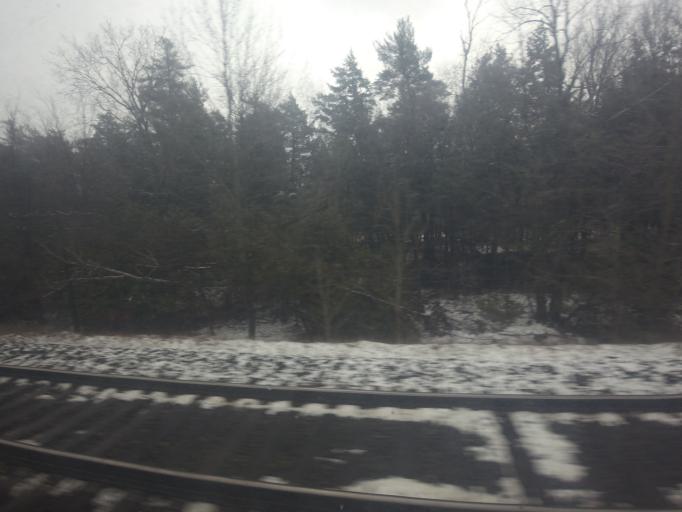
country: CA
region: Ontario
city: Quinte West
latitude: 44.1012
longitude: -77.6135
